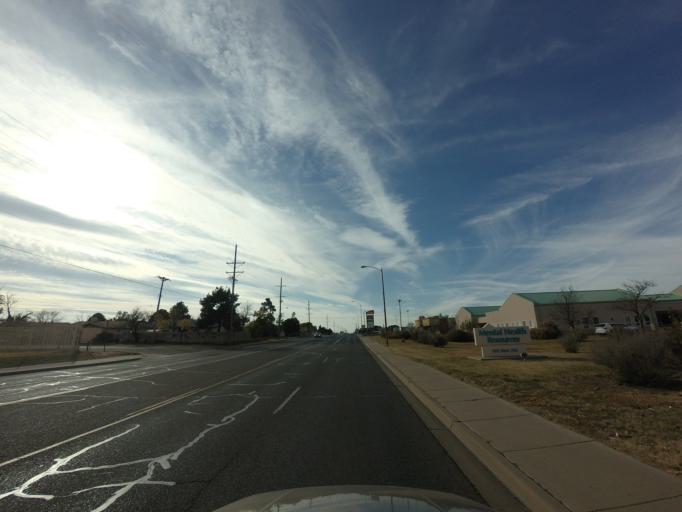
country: US
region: New Mexico
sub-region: Curry County
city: Clovis
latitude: 34.4194
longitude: -103.2181
